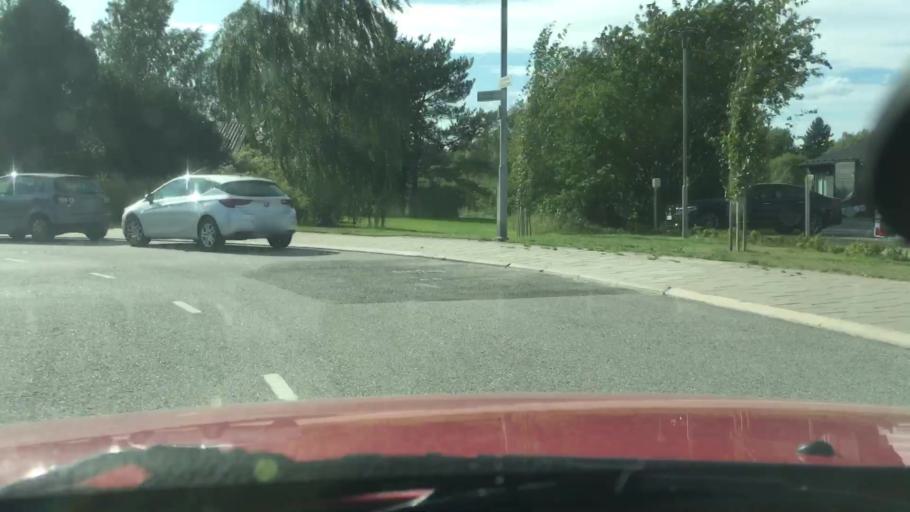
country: FI
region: Varsinais-Suomi
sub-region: Turku
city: Raisio
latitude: 60.4689
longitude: 22.2184
